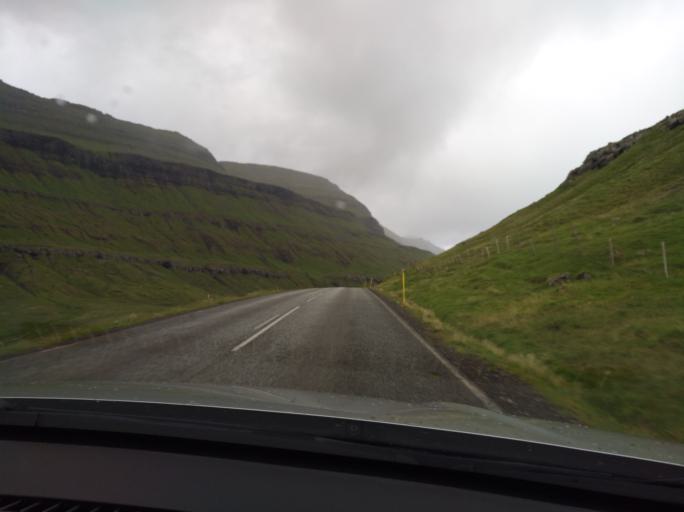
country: FO
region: Eysturoy
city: Fuglafjordur
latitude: 62.2306
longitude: -6.8796
